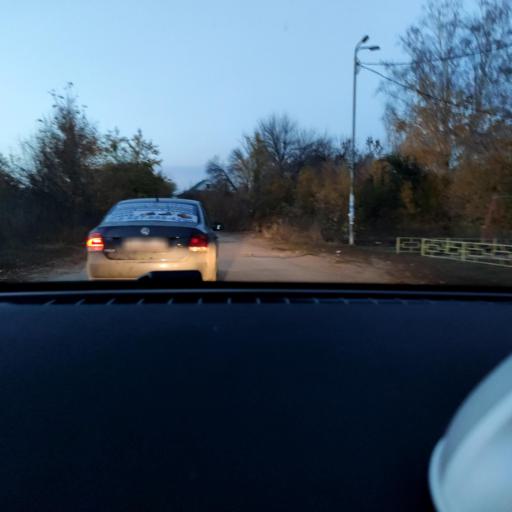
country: RU
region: Samara
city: Petra-Dubrava
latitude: 53.2954
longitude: 50.3046
